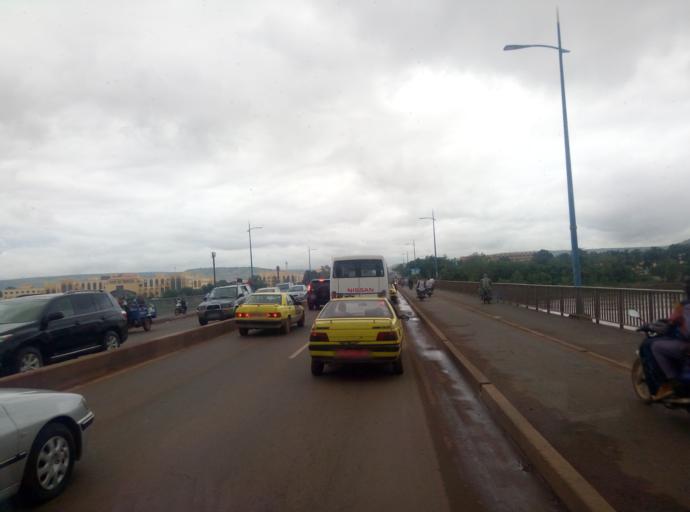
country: ML
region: Bamako
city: Bamako
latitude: 12.6252
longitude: -8.0059
